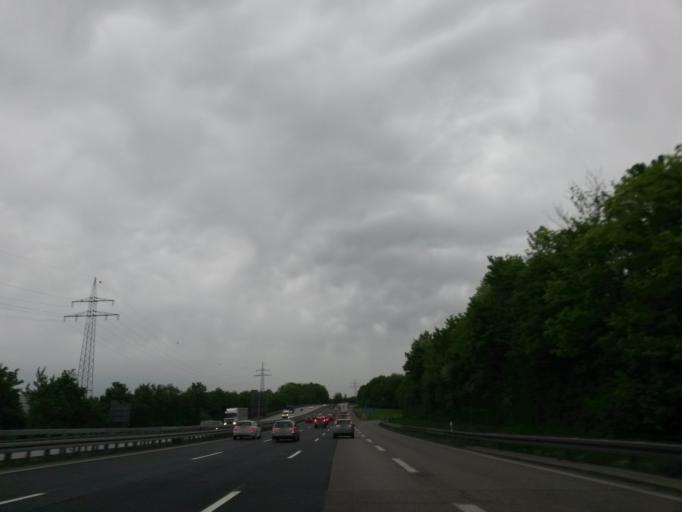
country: DE
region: Baden-Wuerttemberg
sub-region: Regierungsbezirk Stuttgart
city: Ilsfeld
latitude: 49.0535
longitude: 9.2681
